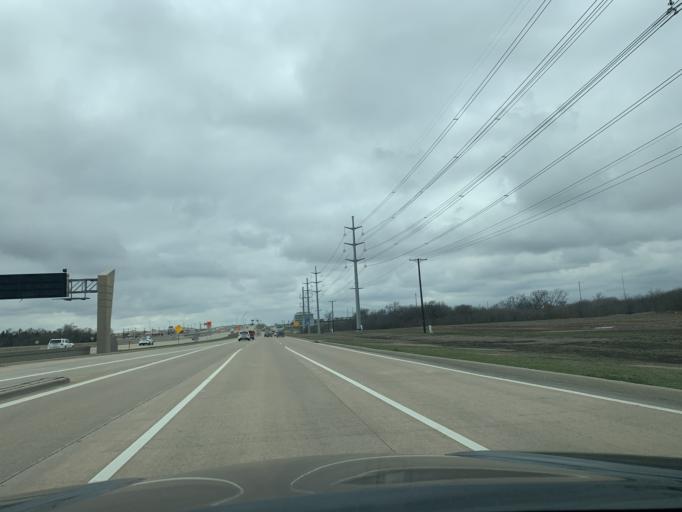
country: US
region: Texas
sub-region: Collin County
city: Fairview
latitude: 33.1489
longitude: -96.6696
